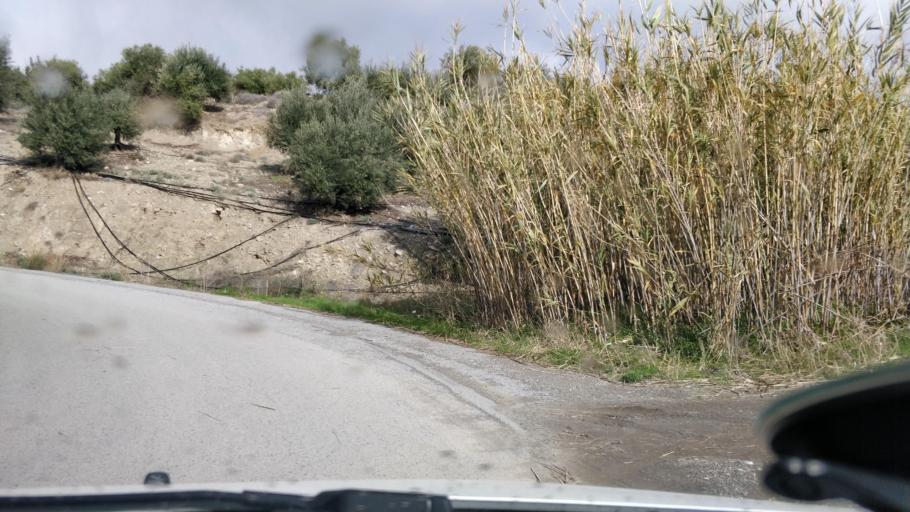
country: GR
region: Crete
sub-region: Nomos Lasithiou
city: Gra Liyia
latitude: 34.9965
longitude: 25.5132
